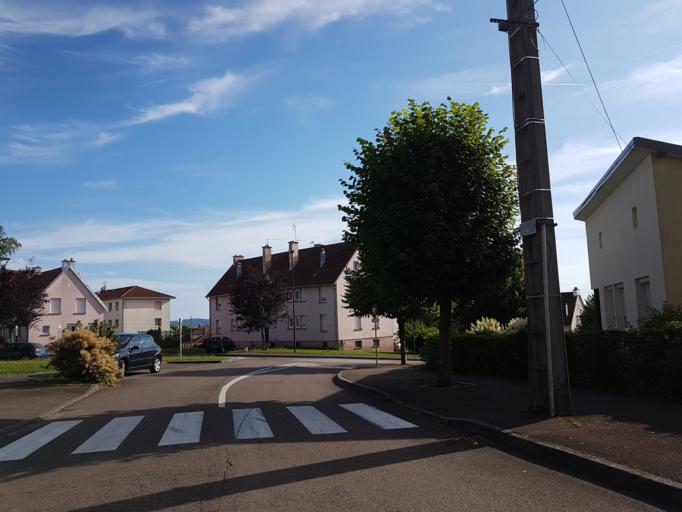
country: FR
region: Franche-Comte
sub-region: Departement de la Haute-Saone
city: Saint-Sauveur
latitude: 47.8197
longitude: 6.3898
